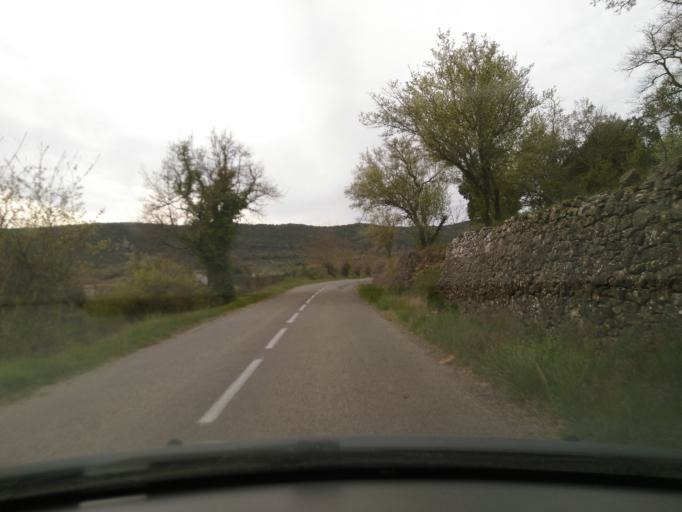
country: FR
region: Rhone-Alpes
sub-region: Departement de l'Ardeche
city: Ruoms
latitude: 44.4327
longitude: 4.4123
